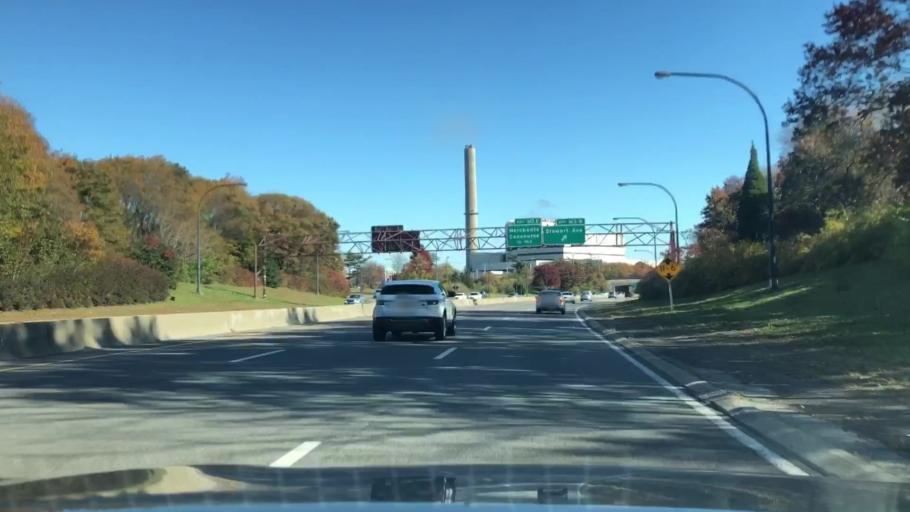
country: US
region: New York
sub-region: Nassau County
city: East Garden City
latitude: 40.7370
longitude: -73.5977
